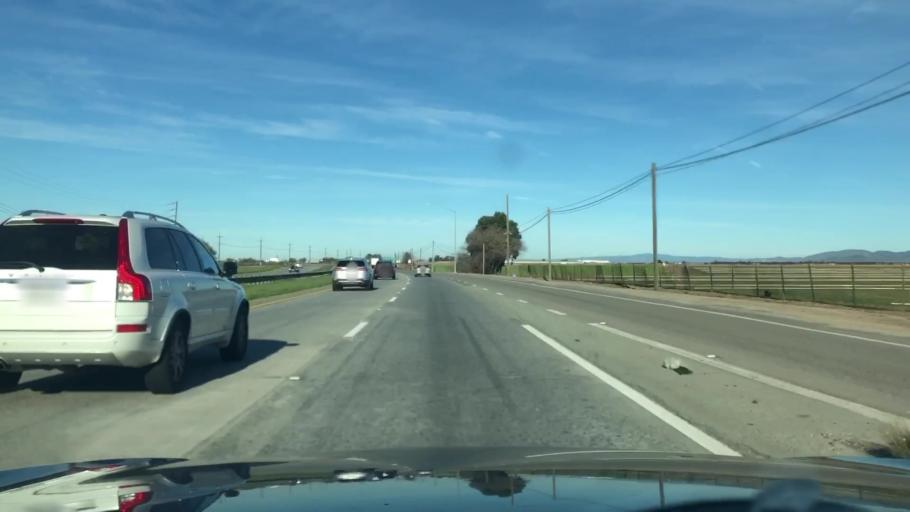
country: US
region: California
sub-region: Monterey County
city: Chualar
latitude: 36.5724
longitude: -121.5210
